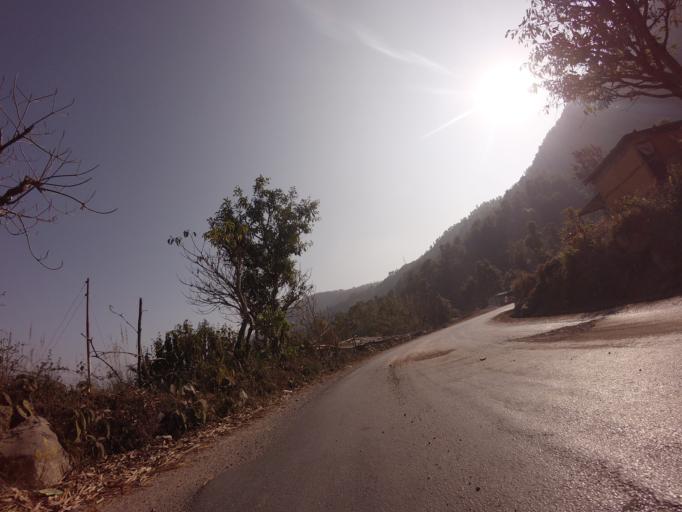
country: NP
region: Western Region
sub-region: Gandaki Zone
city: Pokhara
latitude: 28.1971
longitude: 83.8966
